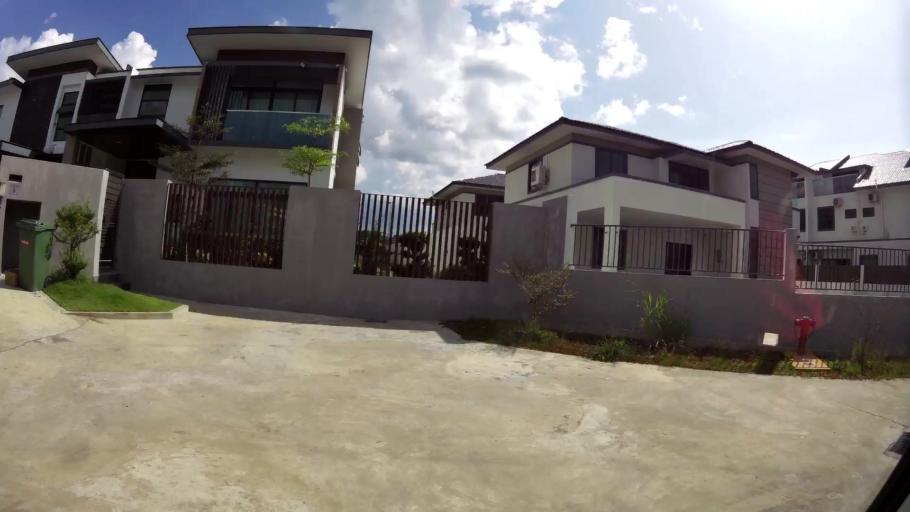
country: BN
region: Brunei and Muara
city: Bandar Seri Begawan
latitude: 4.9519
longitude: 114.9473
